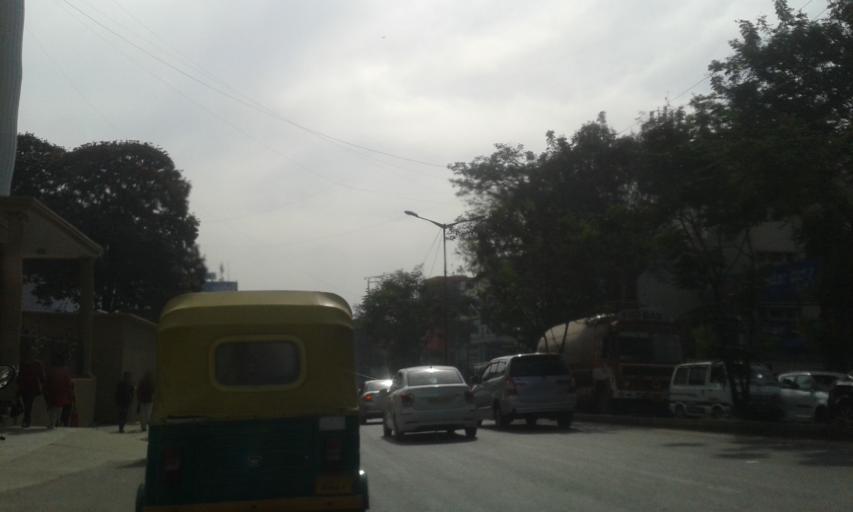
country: IN
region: Karnataka
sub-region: Bangalore Urban
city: Bangalore
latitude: 12.9348
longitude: 77.6099
